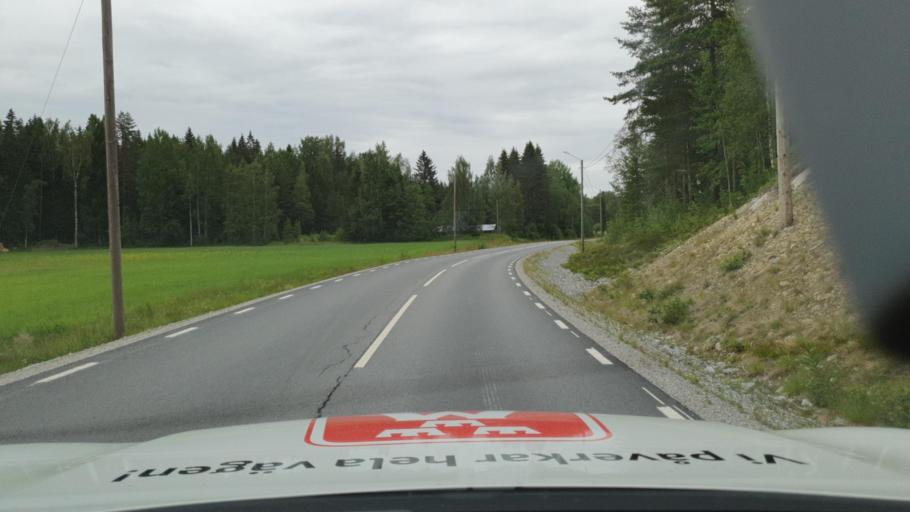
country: SE
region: Vaesterbotten
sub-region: Nordmalings Kommun
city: Nordmaling
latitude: 63.4976
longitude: 19.3205
